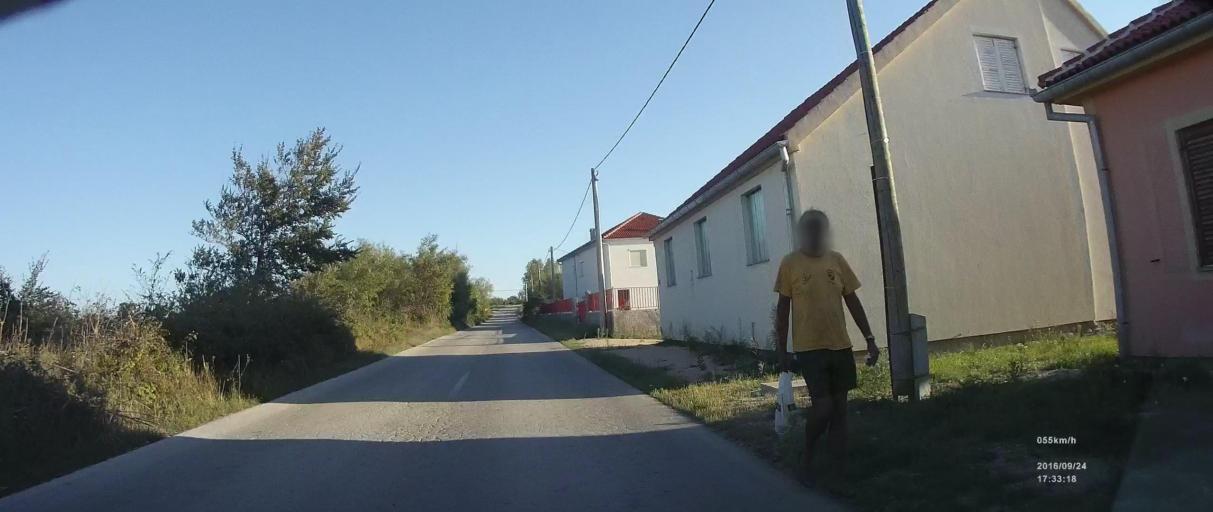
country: HR
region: Zadarska
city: Posedarje
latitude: 44.1755
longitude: 15.4565
